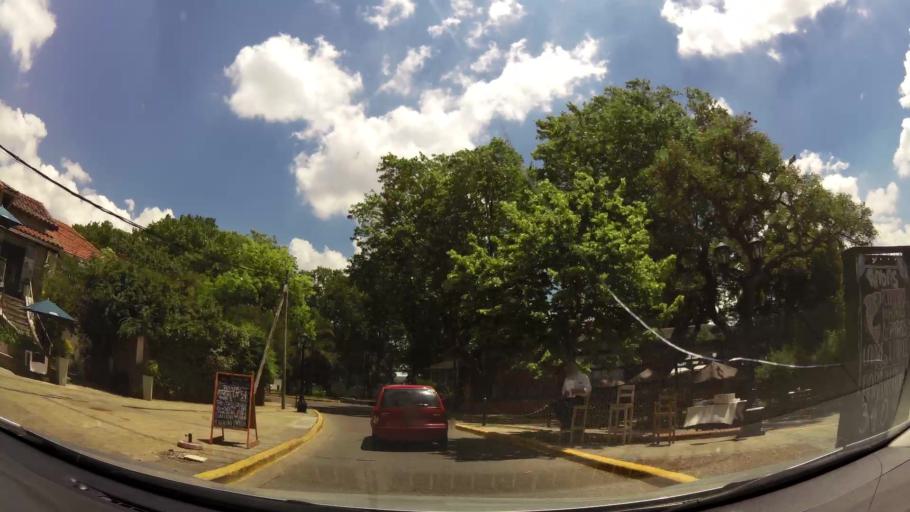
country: AR
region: Buenos Aires
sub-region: Partido de Tigre
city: Tigre
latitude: -34.4139
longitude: -58.5845
